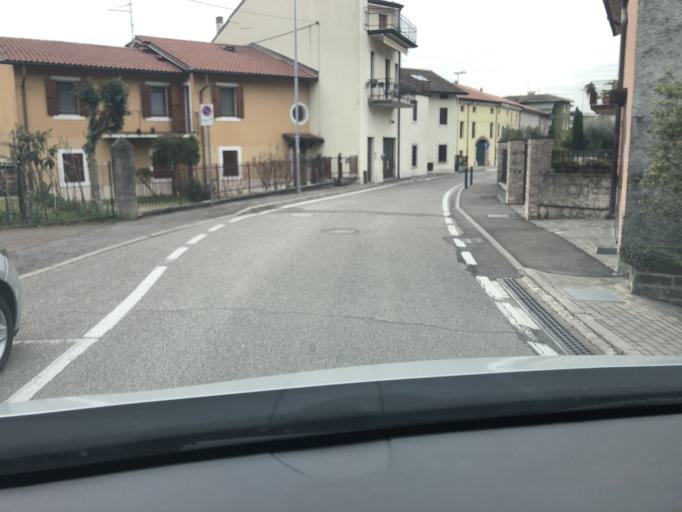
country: IT
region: Veneto
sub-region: Provincia di Verona
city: Sommacampagna
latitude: 45.4066
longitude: 10.8462
